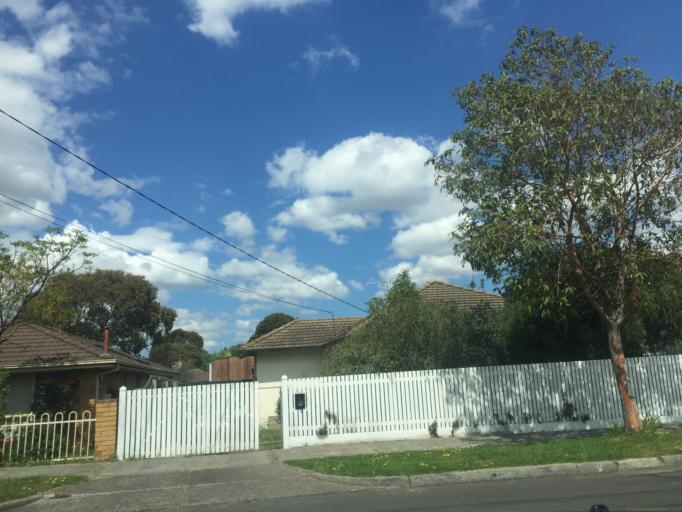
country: AU
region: Victoria
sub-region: Darebin
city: Kingsbury
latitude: -37.7299
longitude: 145.0332
